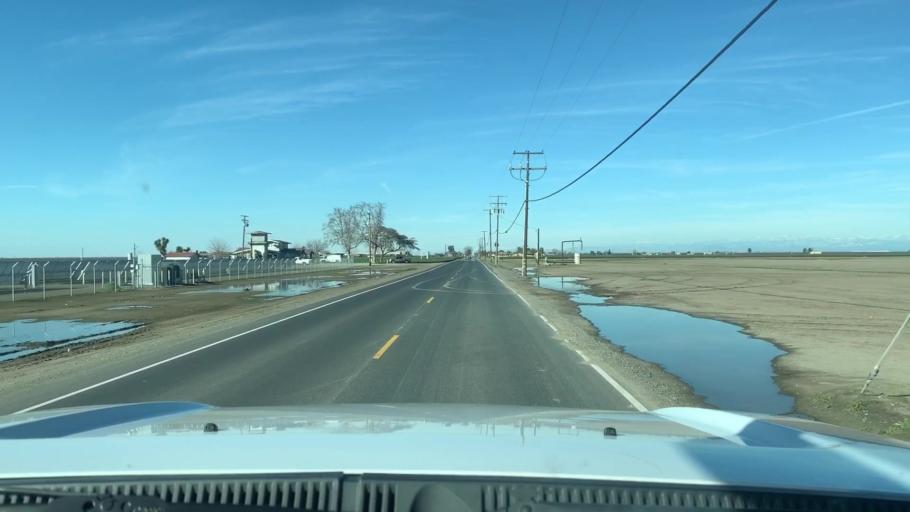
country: US
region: California
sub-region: Kings County
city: Corcoran
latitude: 36.1891
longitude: -119.4932
